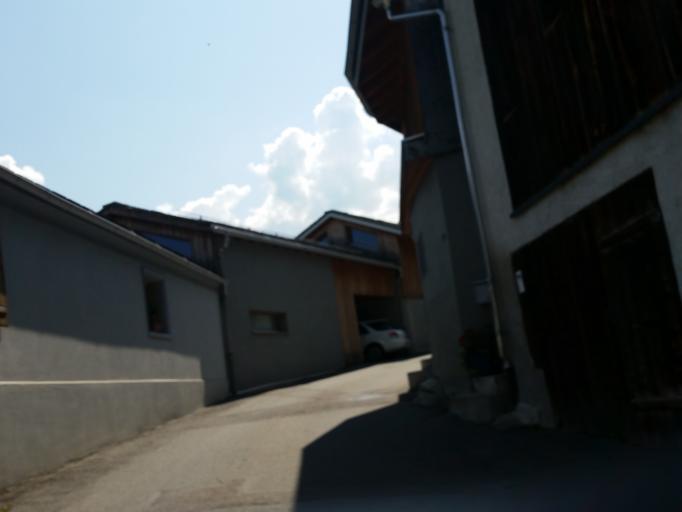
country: CH
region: Valais
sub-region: Martigny District
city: Fully
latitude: 46.1296
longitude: 7.0922
